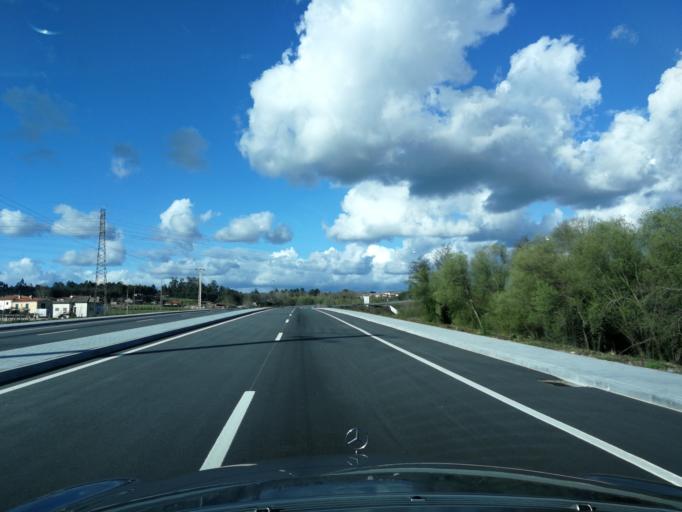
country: PT
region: Braga
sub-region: Braga
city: Braga
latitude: 41.5738
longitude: -8.4404
